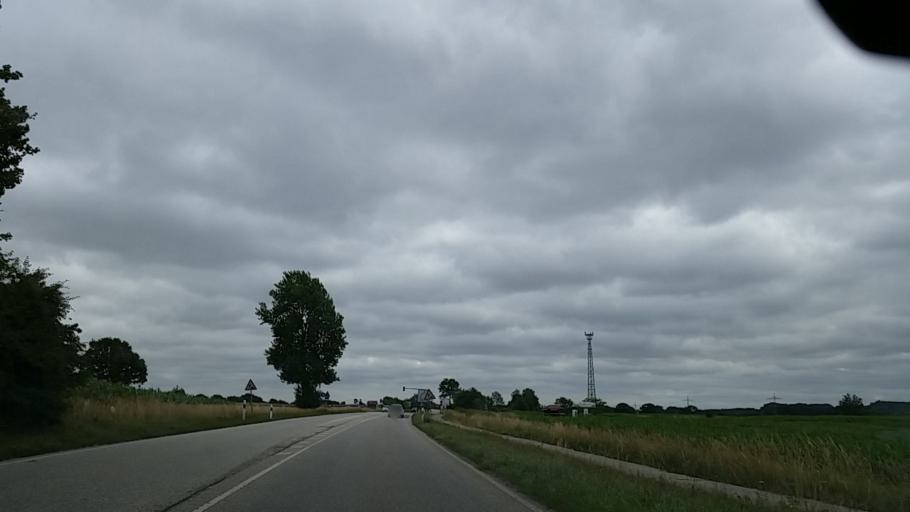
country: DE
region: Schleswig-Holstein
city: Loptin
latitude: 54.1754
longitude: 10.2049
